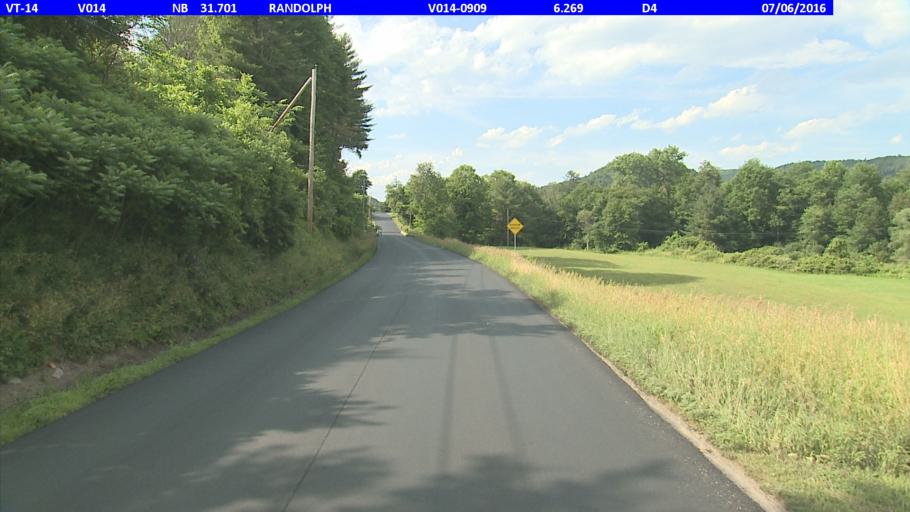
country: US
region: Vermont
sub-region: Orange County
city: Chelsea
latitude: 43.9587
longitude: -72.5511
